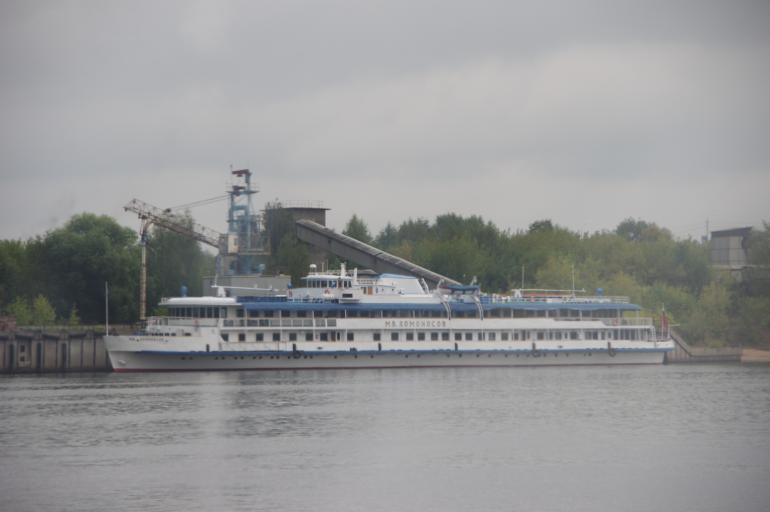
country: RU
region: Jaroslavl
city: Yaroslavl
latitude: 57.6512
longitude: 39.8816
